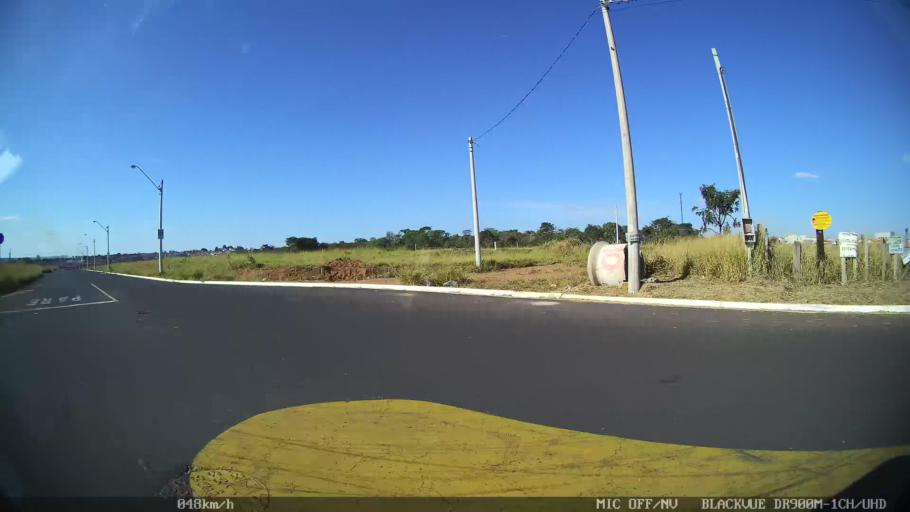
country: BR
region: Sao Paulo
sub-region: Franca
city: Franca
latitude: -20.5071
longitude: -47.4278
